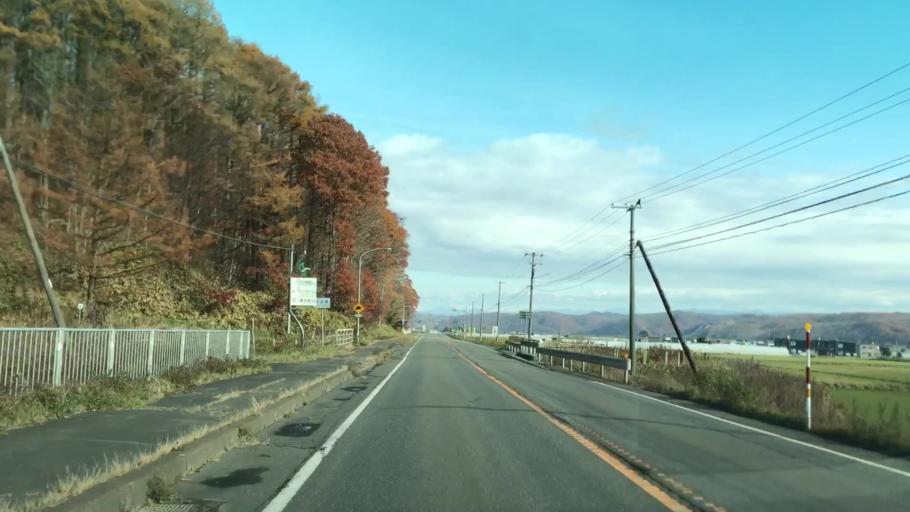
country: JP
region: Hokkaido
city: Shizunai-furukawacho
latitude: 42.5610
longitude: 142.0845
